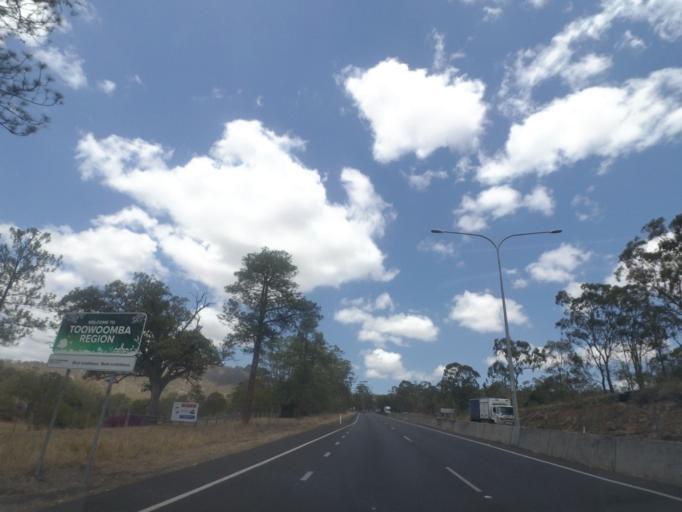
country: AU
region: Queensland
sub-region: Toowoomba
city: East Toowoomba
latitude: -27.5637
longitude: 152.0021
